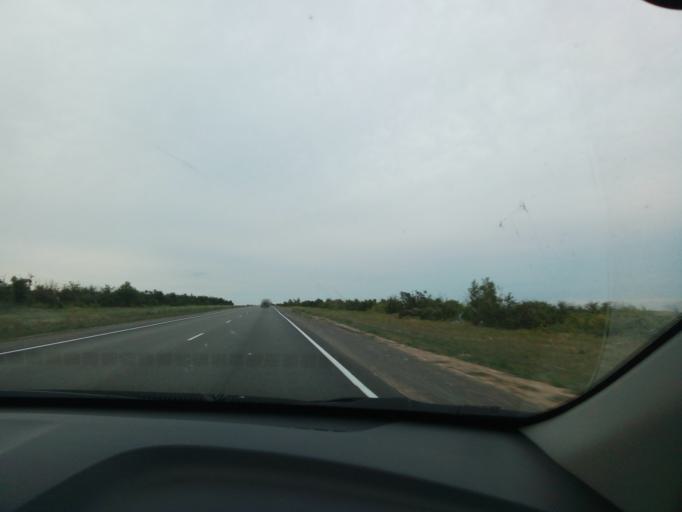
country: RU
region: Volgograd
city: Primorsk
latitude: 49.2045
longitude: 44.8972
